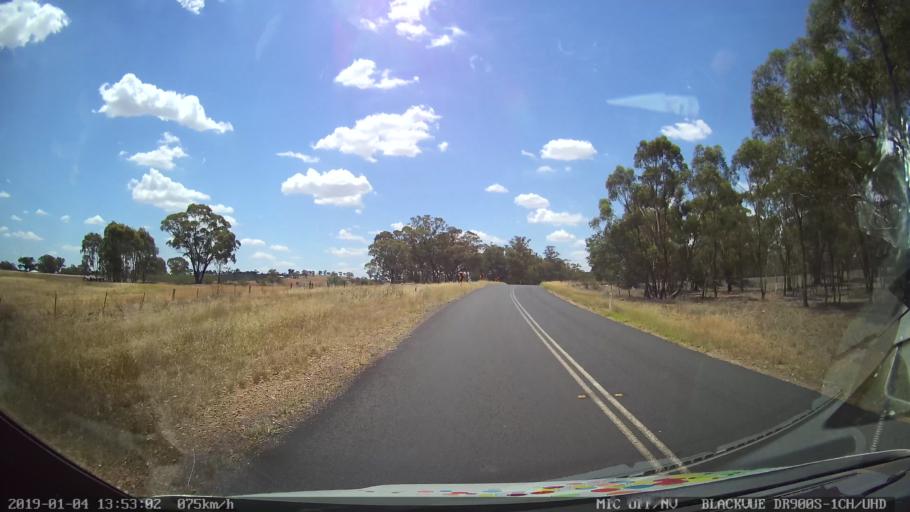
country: AU
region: New South Wales
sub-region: Dubbo Municipality
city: Dubbo
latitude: -32.3874
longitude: 148.5719
